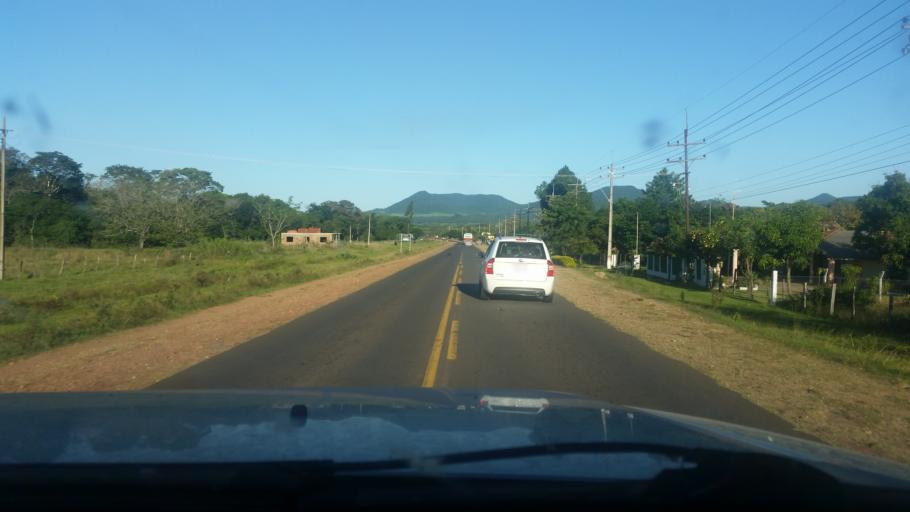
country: PY
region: Guaira
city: Mbocayaty
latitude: -25.7168
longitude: -56.3372
